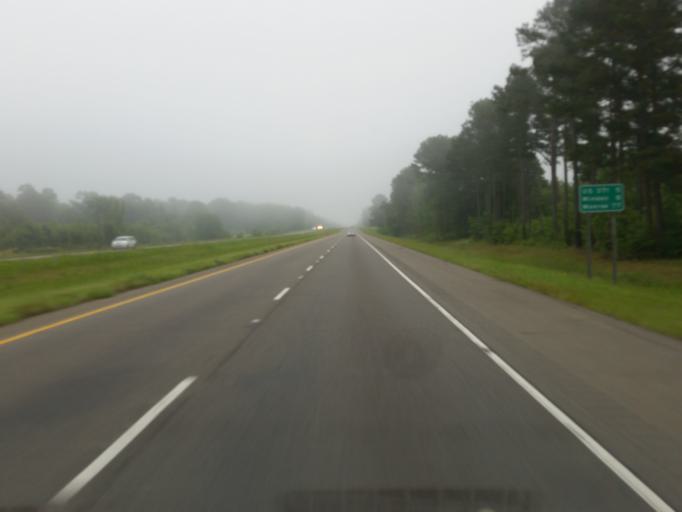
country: US
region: Louisiana
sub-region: Bossier Parish
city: Haughton
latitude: 32.5803
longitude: -93.4166
